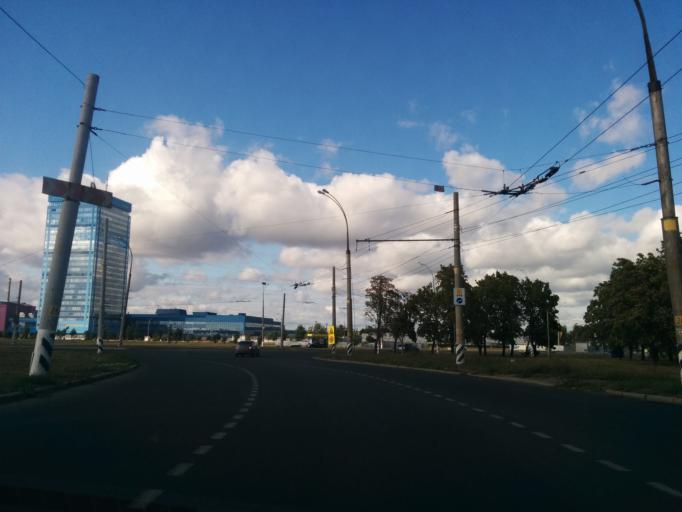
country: RU
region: Samara
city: Tol'yatti
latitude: 53.5522
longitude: 49.2681
